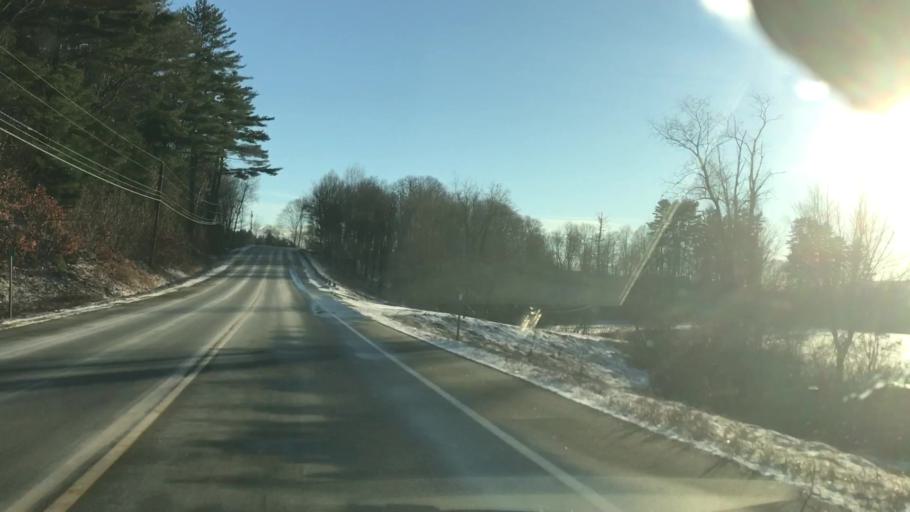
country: US
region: New Hampshire
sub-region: Grafton County
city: Orford
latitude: 43.8893
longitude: -72.1507
